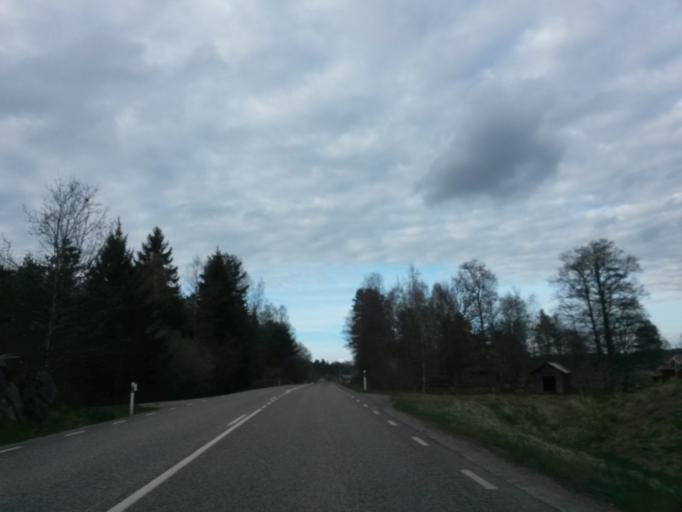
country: SE
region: Vaestra Goetaland
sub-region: Vargarda Kommun
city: Jonstorp
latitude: 58.0442
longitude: 12.6509
